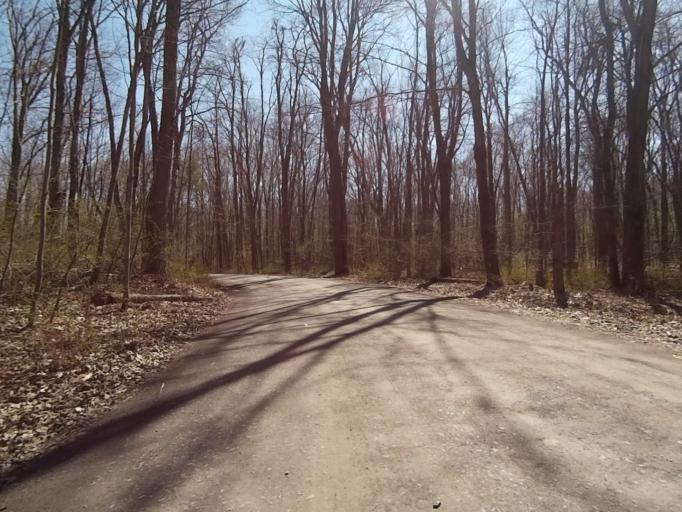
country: US
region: Pennsylvania
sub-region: Centre County
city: Park Forest Village
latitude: 40.8061
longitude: -77.9448
